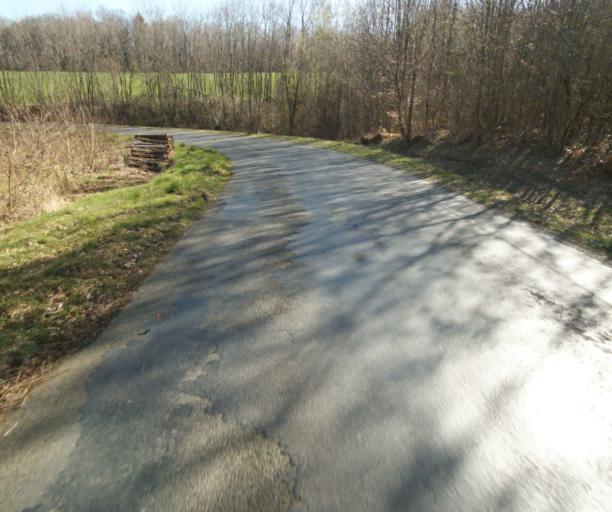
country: FR
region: Limousin
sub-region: Departement de la Correze
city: Seilhac
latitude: 45.3969
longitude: 1.7471
